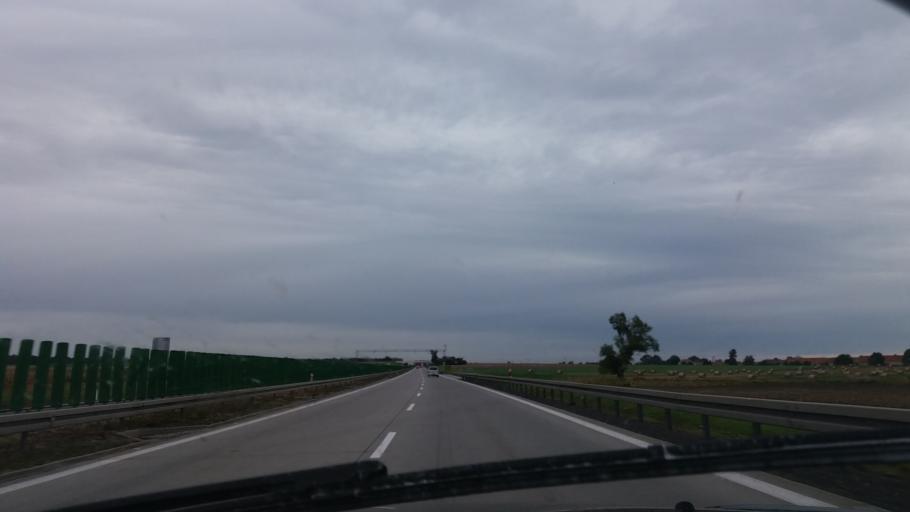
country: PL
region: Lower Silesian Voivodeship
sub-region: Powiat sredzki
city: Udanin
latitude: 51.1105
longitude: 16.3942
